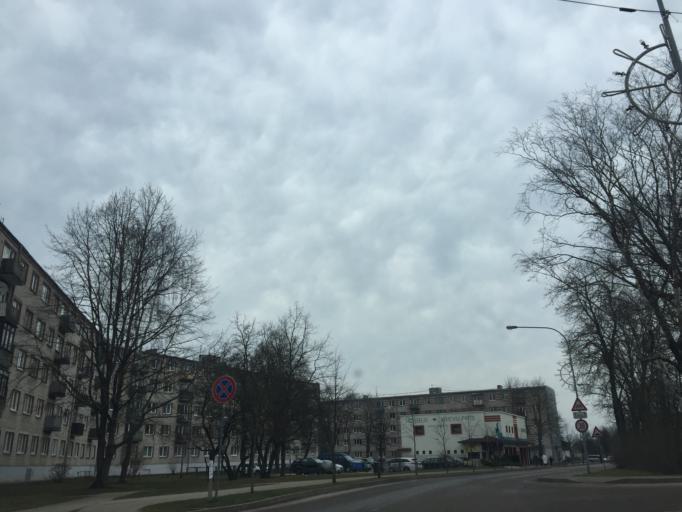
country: LV
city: Tireli
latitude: 56.9607
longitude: 23.6094
